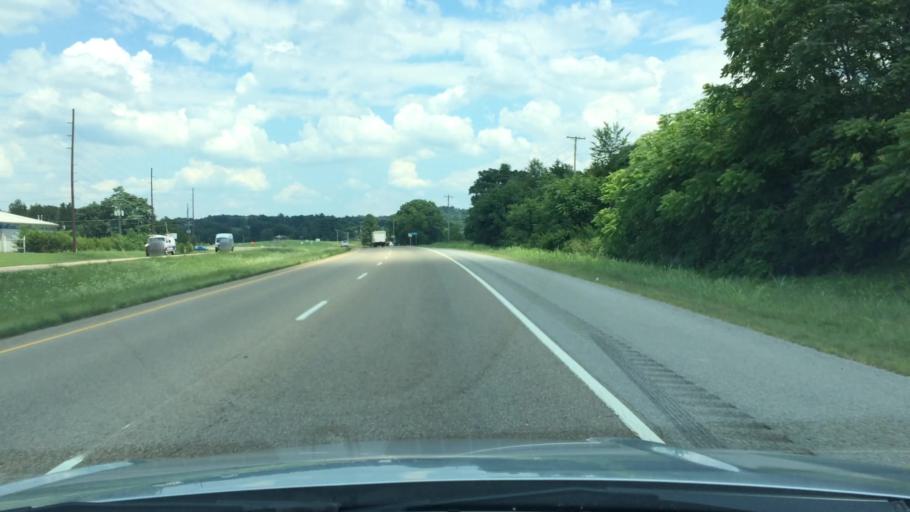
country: US
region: Tennessee
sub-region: Hamblen County
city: Morristown
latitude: 36.1655
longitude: -83.3728
